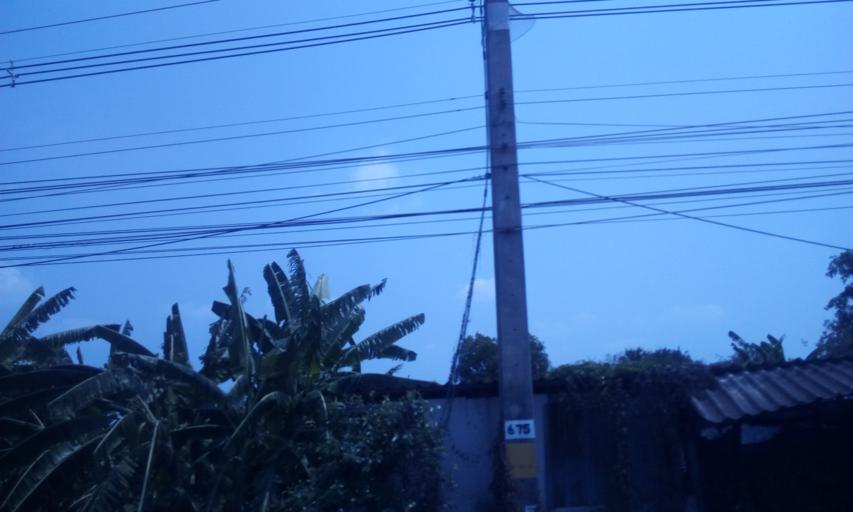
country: TH
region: Chachoengsao
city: Bang Nam Priao
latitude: 13.8217
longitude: 101.0536
